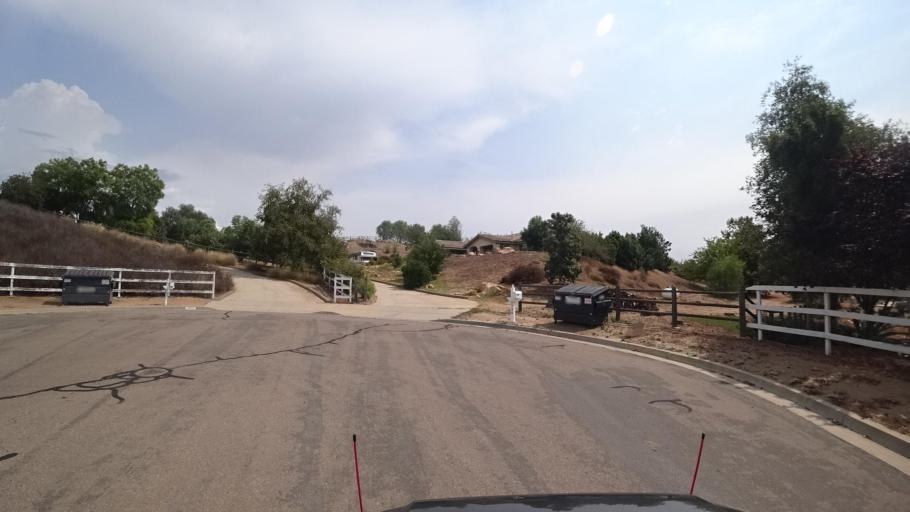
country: US
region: California
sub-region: San Diego County
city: Ramona
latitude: 33.0041
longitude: -116.8939
